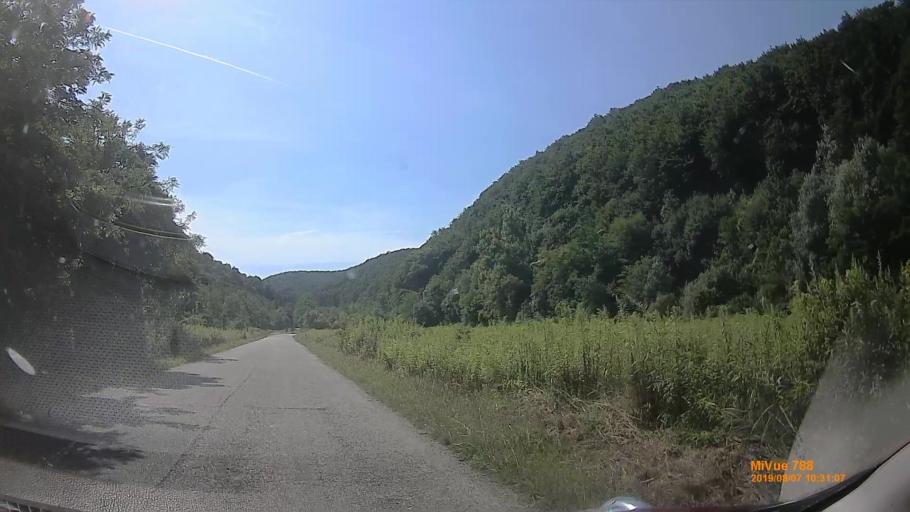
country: HU
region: Veszprem
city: Ajka
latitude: 47.0731
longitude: 17.5820
